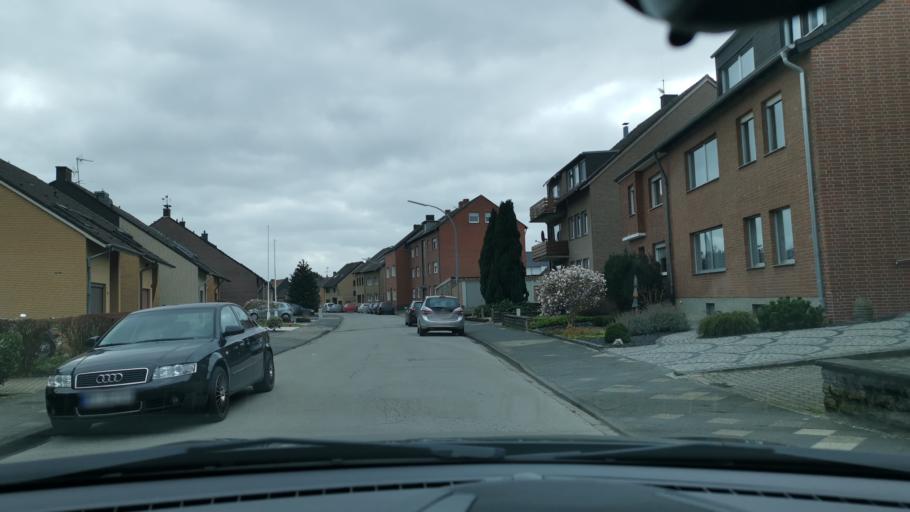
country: DE
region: North Rhine-Westphalia
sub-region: Regierungsbezirk Dusseldorf
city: Grevenbroich
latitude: 51.0746
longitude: 6.5710
